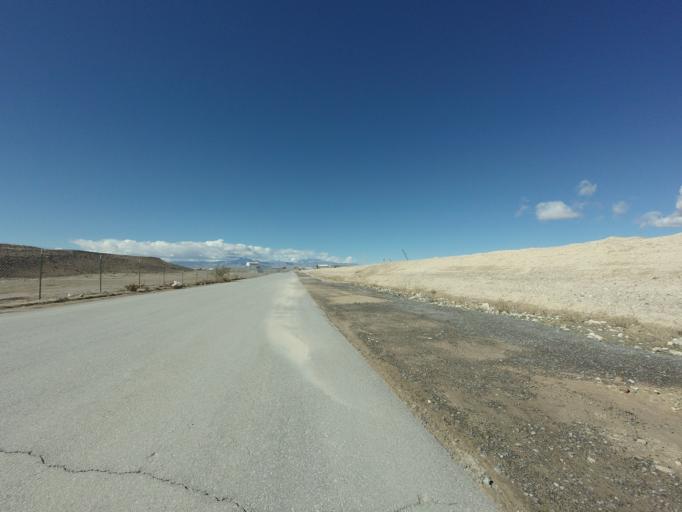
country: US
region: Nevada
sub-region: Clark County
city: Nellis Air Force Base
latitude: 36.2583
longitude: -115.0263
